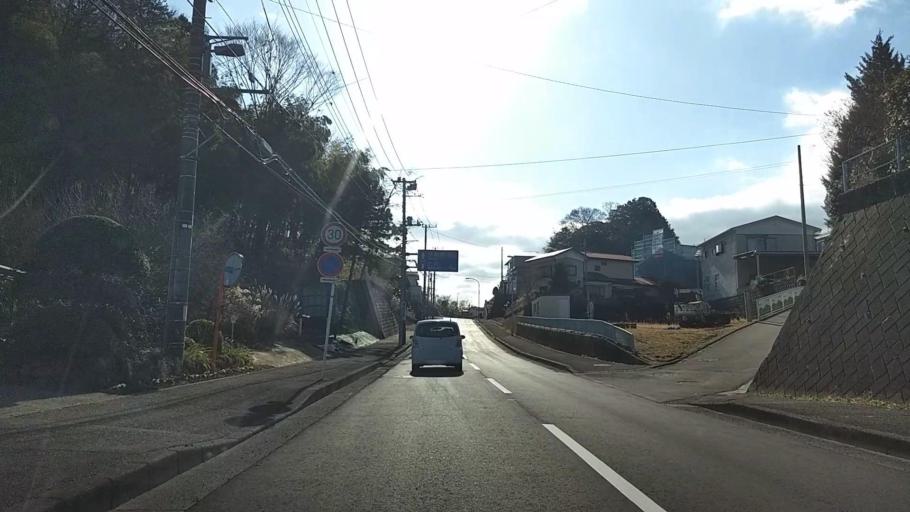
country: JP
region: Kanagawa
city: Atsugi
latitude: 35.4722
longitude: 139.2869
